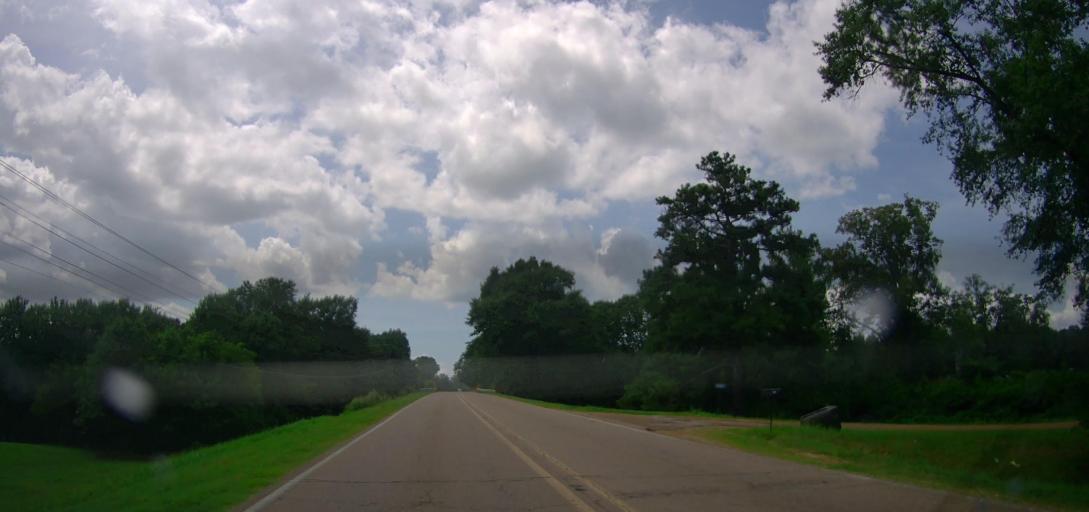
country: US
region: Mississippi
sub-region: Lee County
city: Shannon
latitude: 34.1200
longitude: -88.7092
